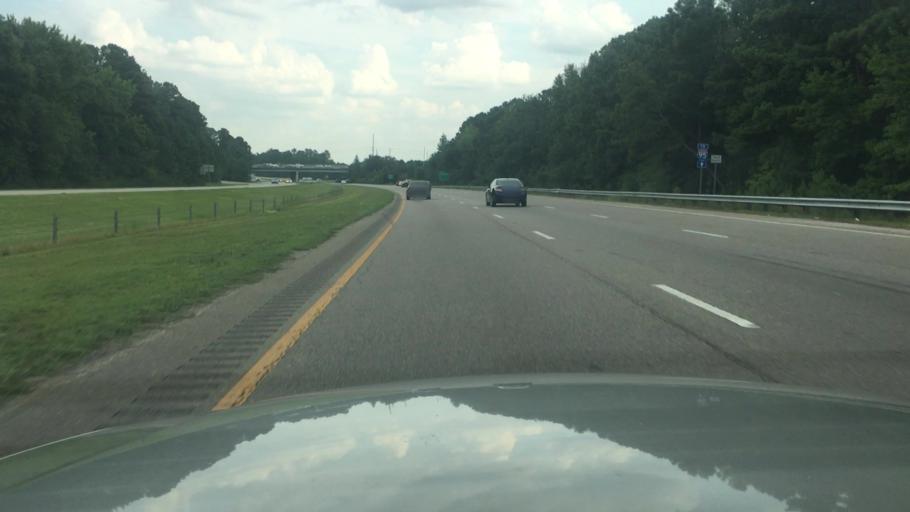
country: US
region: North Carolina
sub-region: Cumberland County
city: Fayetteville
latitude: 35.0633
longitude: -78.9557
